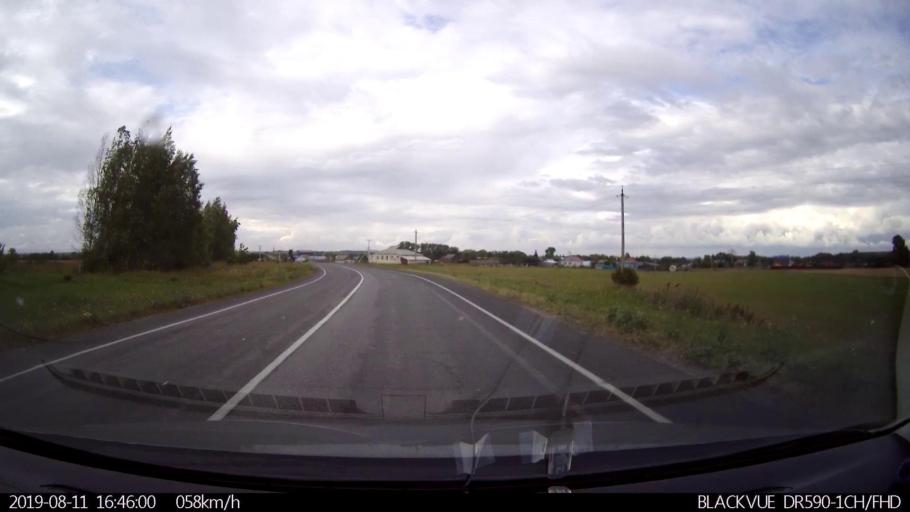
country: RU
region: Ulyanovsk
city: Mayna
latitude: 54.1948
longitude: 47.6886
